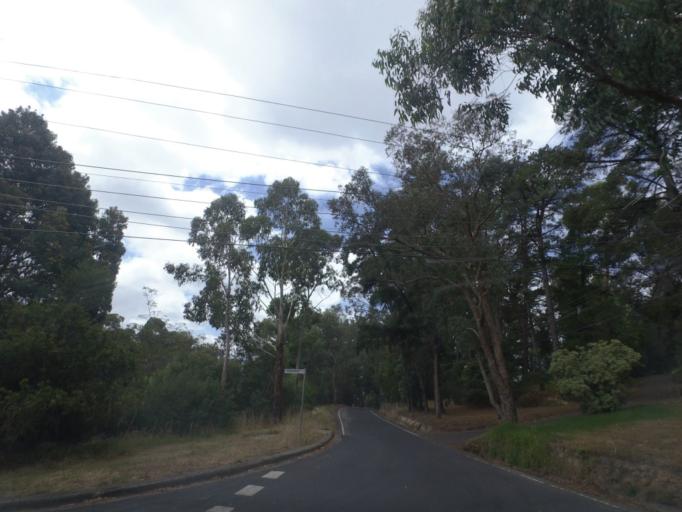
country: AU
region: Victoria
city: Mitcham
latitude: -37.7985
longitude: 145.2074
